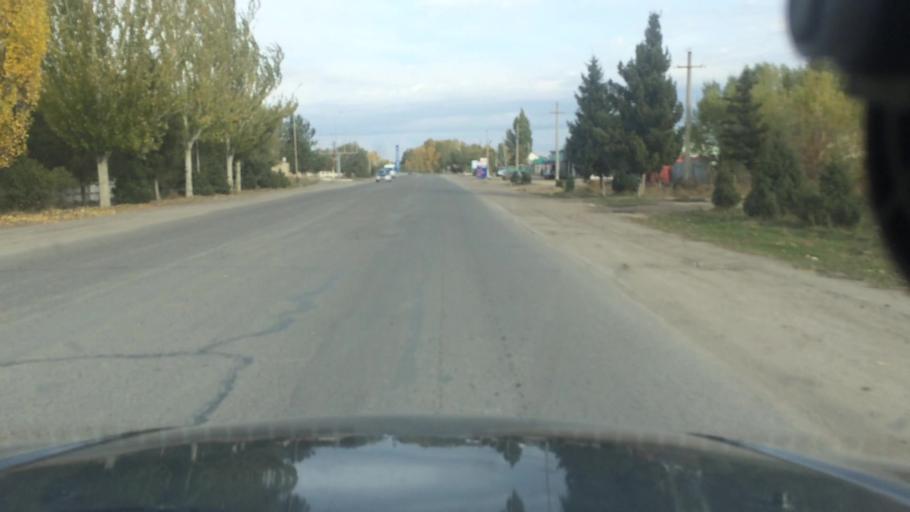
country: KG
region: Ysyk-Koel
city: Karakol
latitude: 42.5294
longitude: 78.3833
